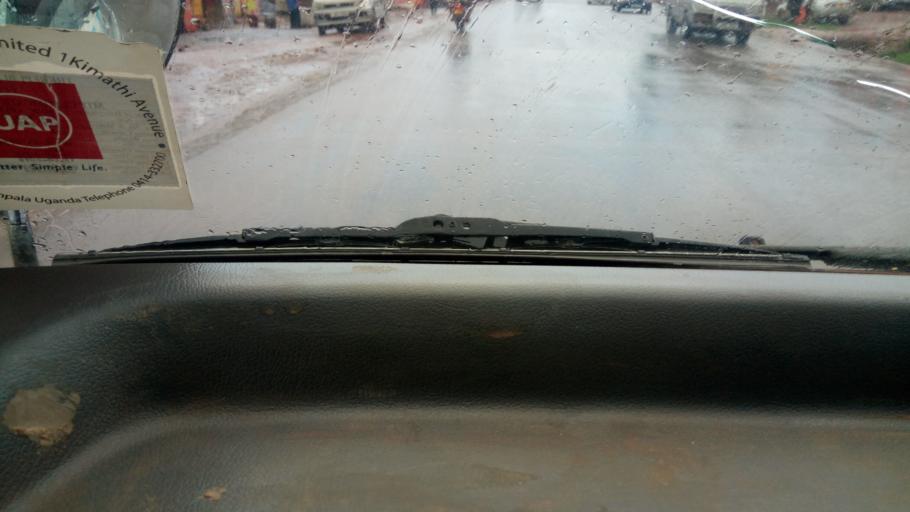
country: UG
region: Central Region
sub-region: Wakiso District
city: Wakiso
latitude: 0.3824
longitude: 32.5184
